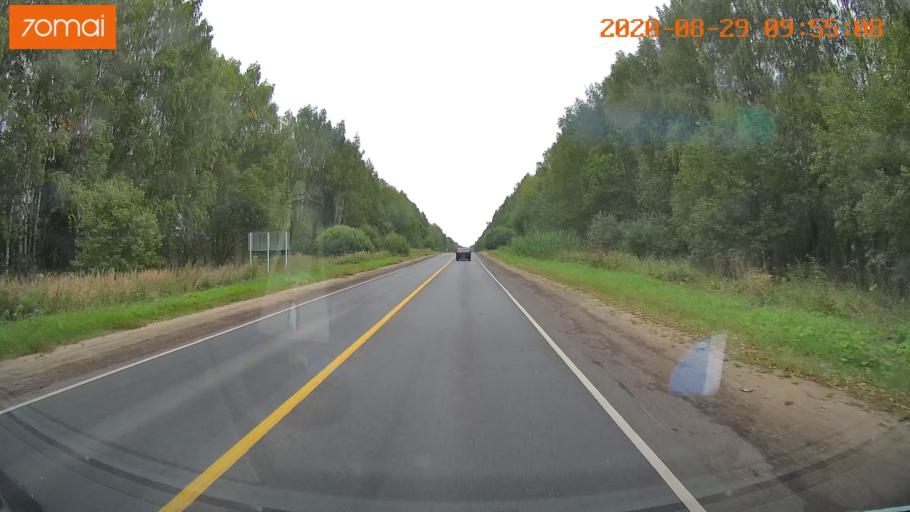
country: RU
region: Ivanovo
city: Zarechnyy
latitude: 57.4227
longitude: 42.2555
